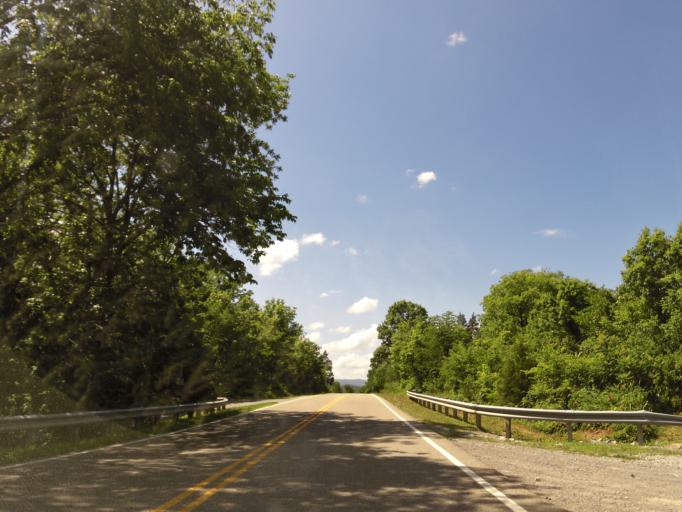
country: US
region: Virginia
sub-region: Lee County
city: Pennington Gap
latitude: 36.7221
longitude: -82.9848
